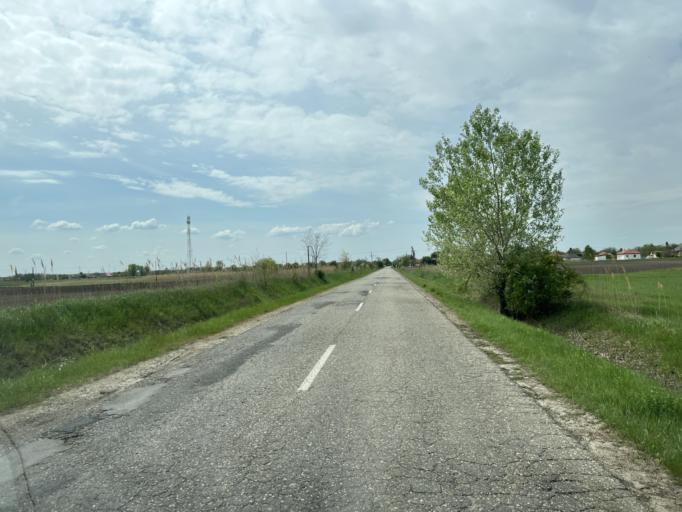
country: HU
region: Pest
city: Tortel
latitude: 47.1283
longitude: 19.9455
